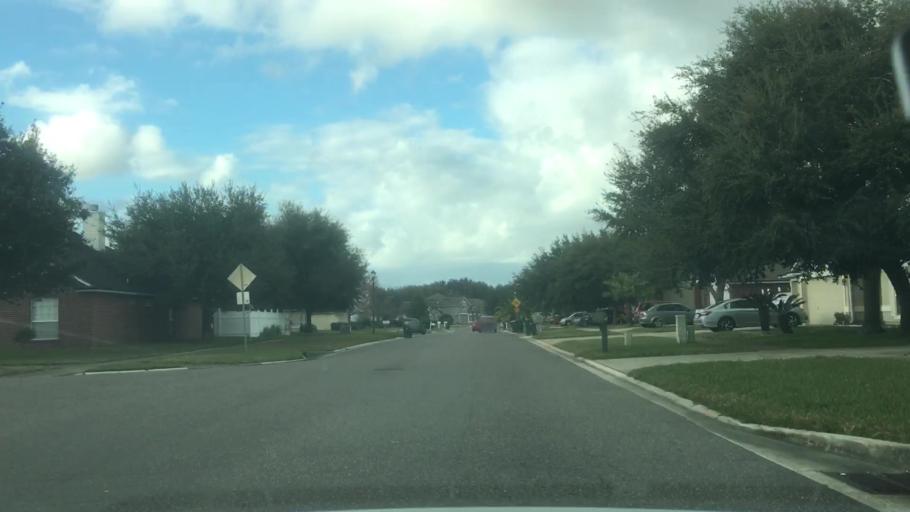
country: US
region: Florida
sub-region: Duval County
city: Neptune Beach
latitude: 30.3069
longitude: -81.5052
